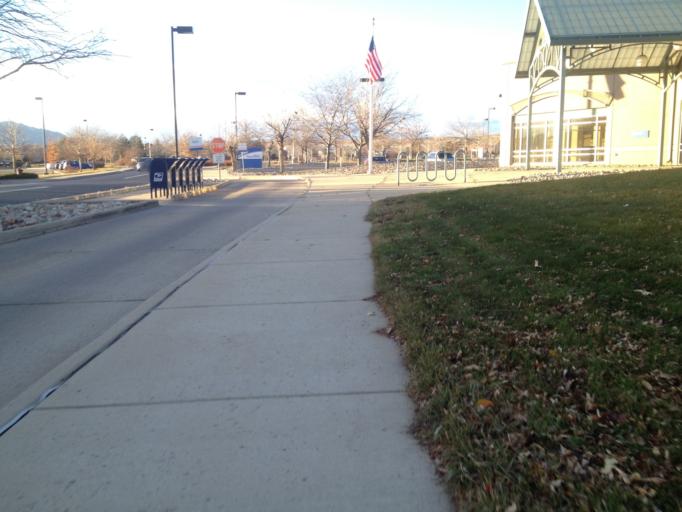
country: US
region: Colorado
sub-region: Boulder County
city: Superior
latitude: 39.9612
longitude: -105.1600
